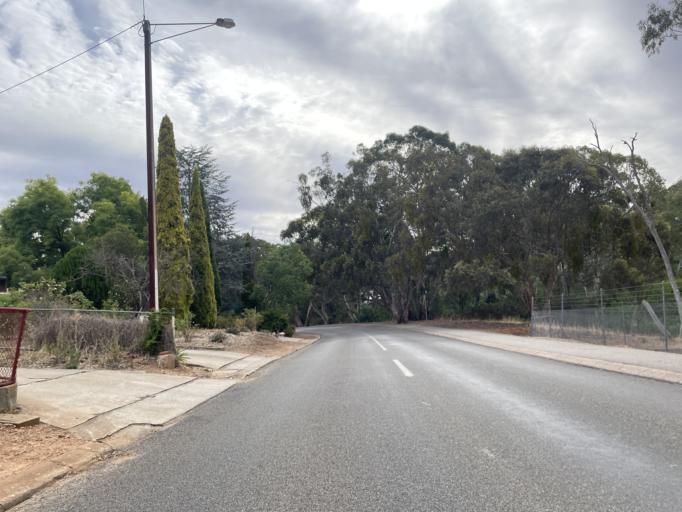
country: AU
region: South Australia
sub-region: Clare and Gilbert Valleys
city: Clare
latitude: -33.8409
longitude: 138.6141
